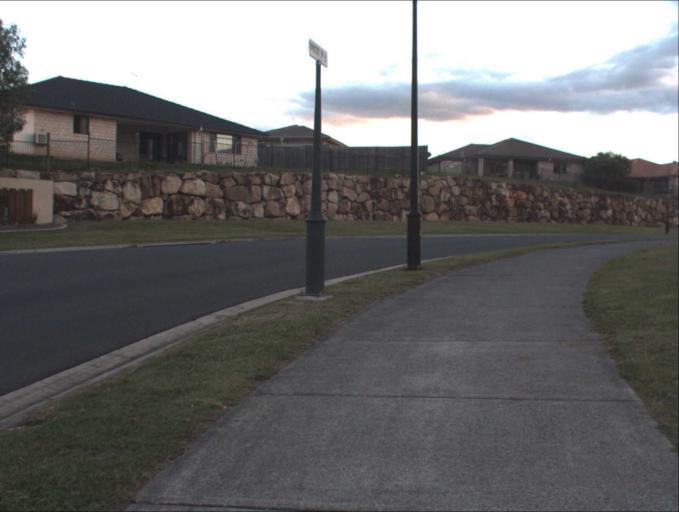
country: AU
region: Queensland
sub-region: Logan
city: North Maclean
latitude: -27.8020
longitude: 152.9573
